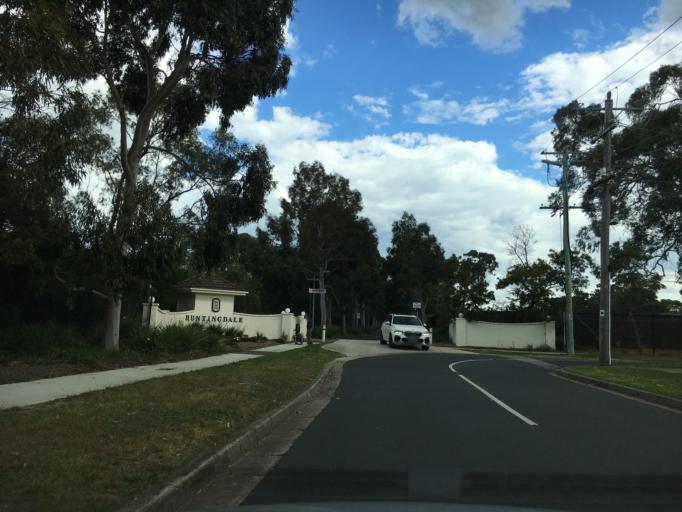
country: AU
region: Victoria
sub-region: Monash
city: Oakleigh South
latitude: -37.9140
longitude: 145.0984
